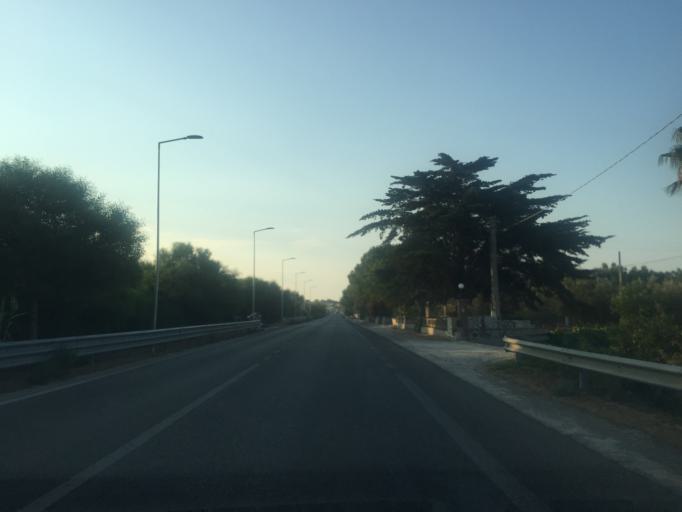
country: IT
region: Sicily
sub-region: Ragusa
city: Cava d'Aliga
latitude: 36.7228
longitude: 14.7502
